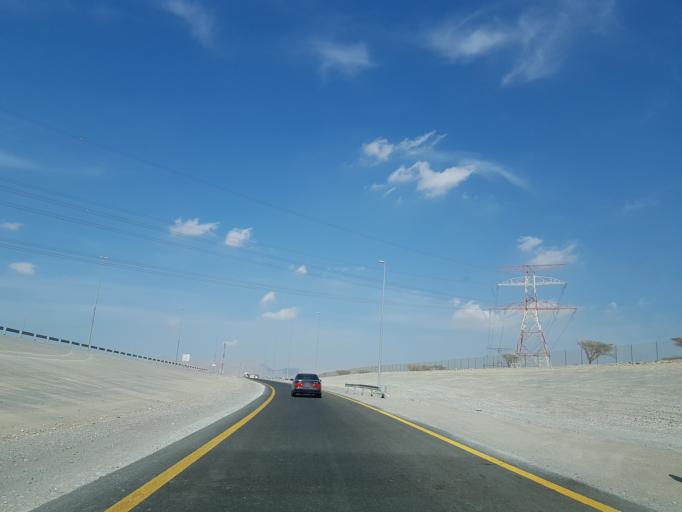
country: AE
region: Ra's al Khaymah
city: Ras al-Khaimah
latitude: 25.7644
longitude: 56.0239
